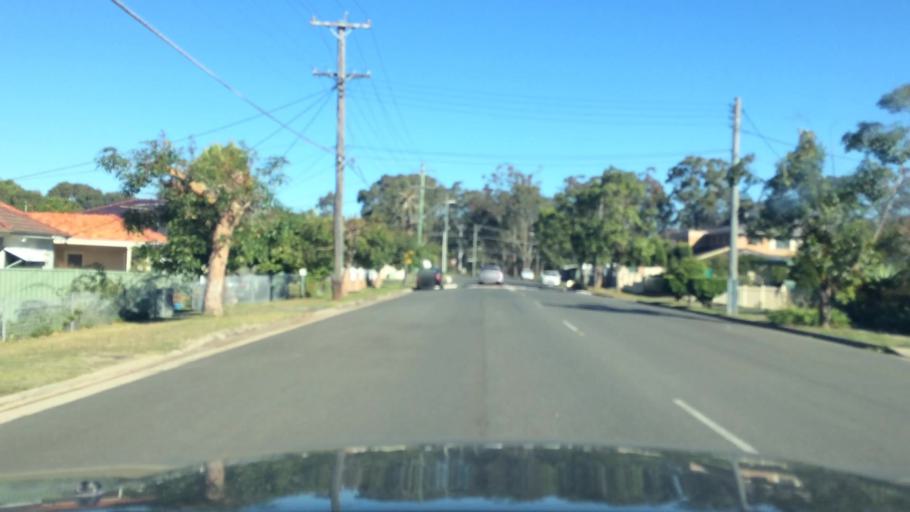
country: AU
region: New South Wales
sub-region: Fairfield
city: Carramar
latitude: -33.8771
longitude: 150.9551
